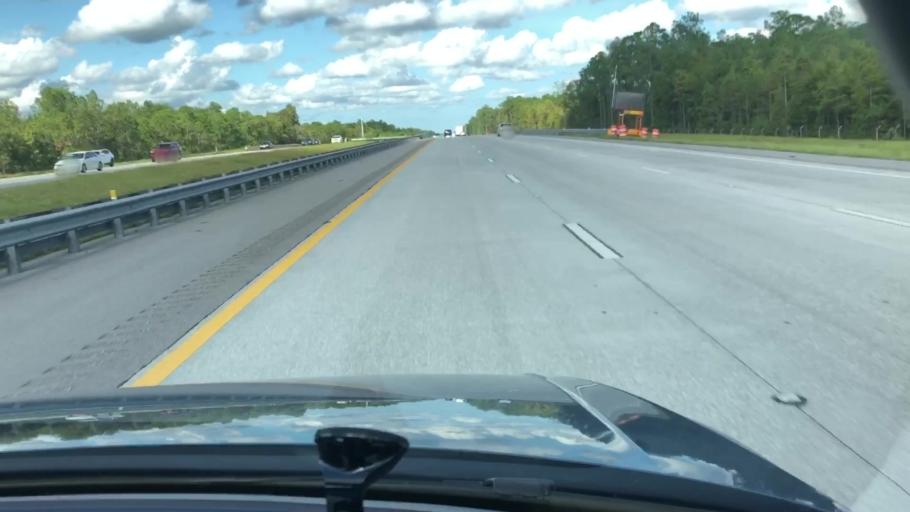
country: US
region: Florida
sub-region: Volusia County
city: Samsula-Spruce Creek
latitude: 29.0986
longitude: -81.1547
